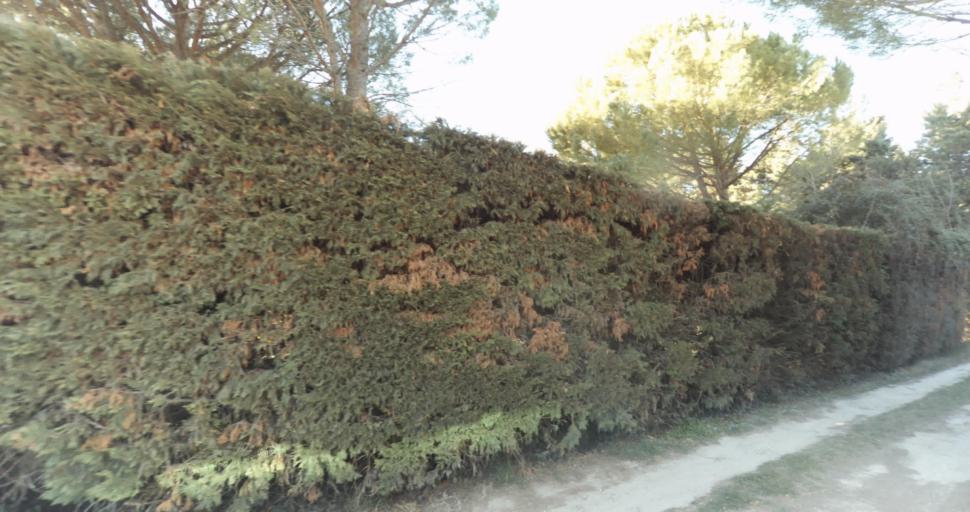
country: FR
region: Provence-Alpes-Cote d'Azur
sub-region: Departement des Bouches-du-Rhone
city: Barbentane
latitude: 43.9053
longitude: 4.7413
